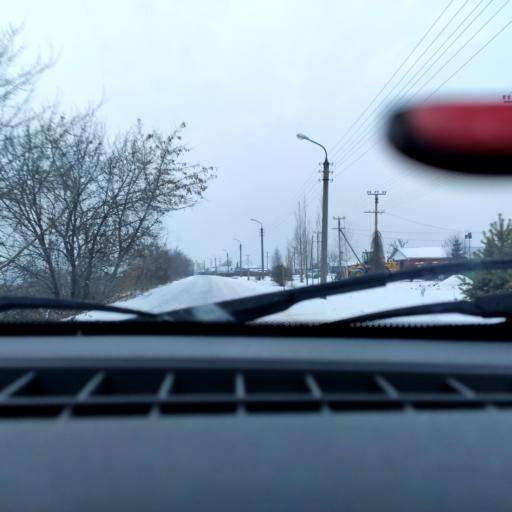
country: RU
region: Bashkortostan
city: Blagoveshchensk
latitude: 54.8924
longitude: 56.0315
